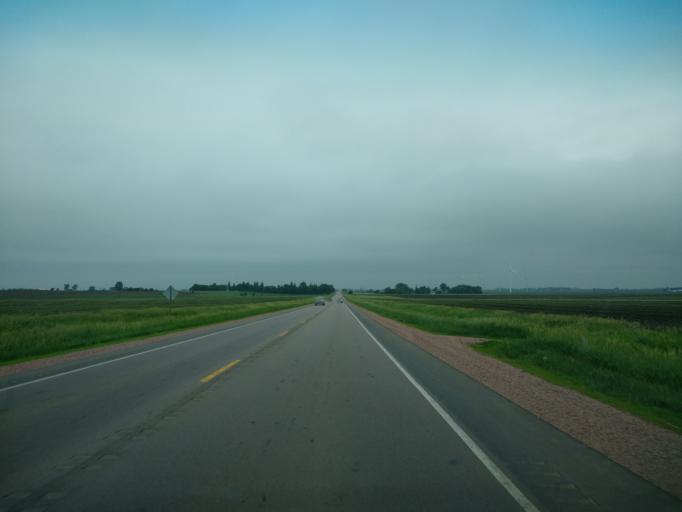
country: US
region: Iowa
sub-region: O'Brien County
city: Sanborn
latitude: 43.1861
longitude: -95.6684
